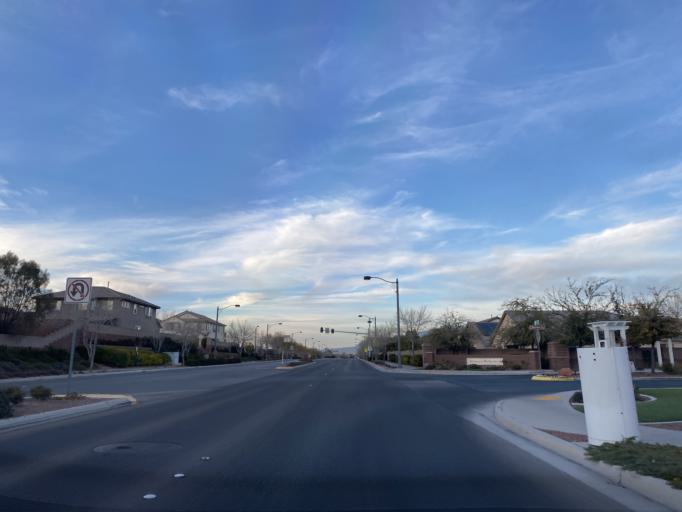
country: US
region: Nevada
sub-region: Clark County
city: Summerlin South
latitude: 36.2944
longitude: -115.3195
